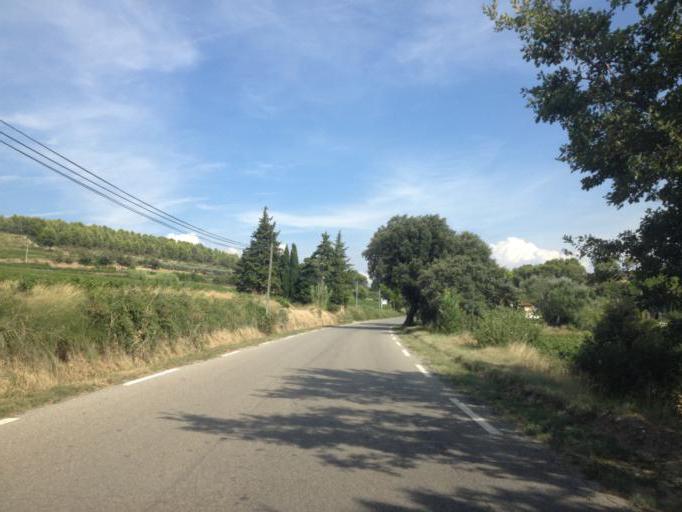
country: FR
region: Provence-Alpes-Cote d'Azur
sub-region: Departement du Vaucluse
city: Vacqueyras
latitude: 44.1383
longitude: 4.9970
